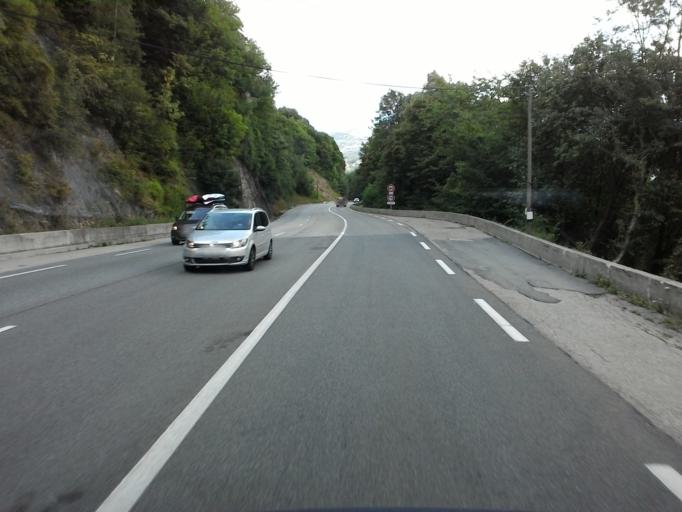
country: FR
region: Rhone-Alpes
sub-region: Departement de l'Isere
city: Notre-Dame-de-Mesage
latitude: 45.0508
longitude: 5.7535
